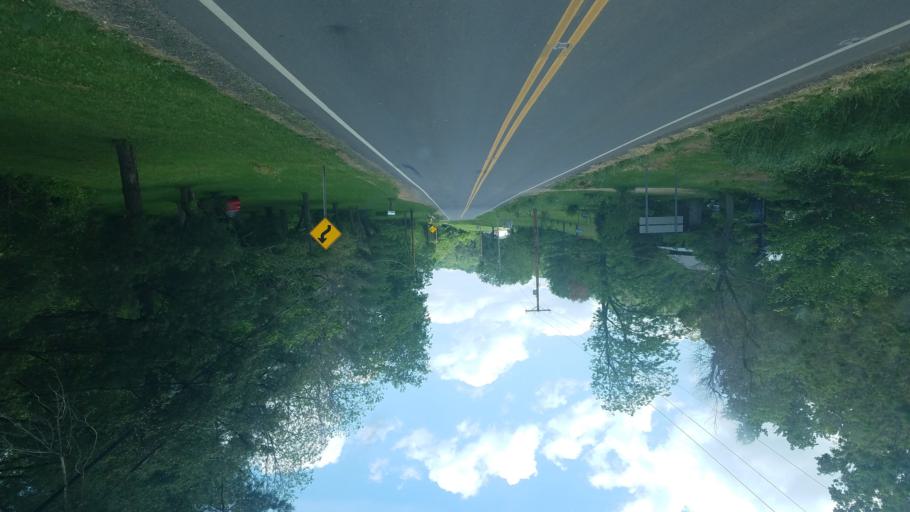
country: US
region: Ohio
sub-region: Meigs County
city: Pomeroy
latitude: 39.0397
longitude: -82.0620
